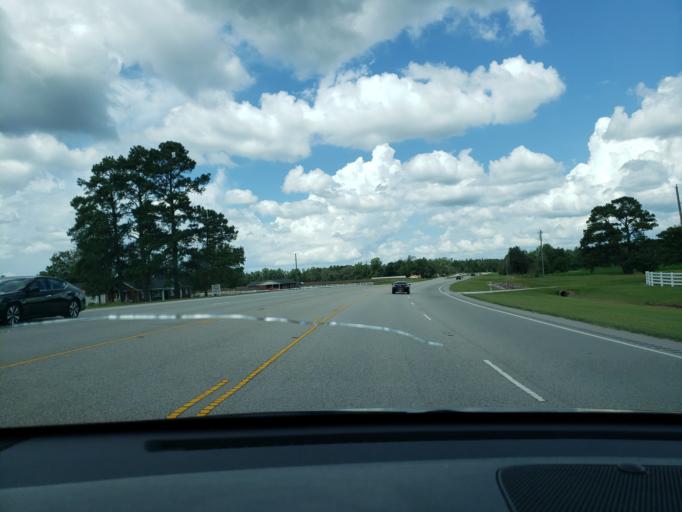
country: US
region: North Carolina
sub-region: Bladen County
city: Elizabethtown
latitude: 34.6737
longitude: -78.7387
